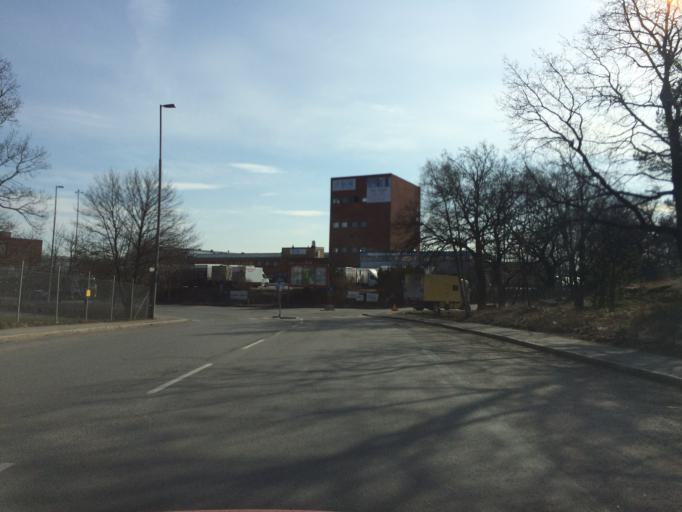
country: SE
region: Stockholm
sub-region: Stockholms Kommun
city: Arsta
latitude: 59.2916
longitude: 18.0099
